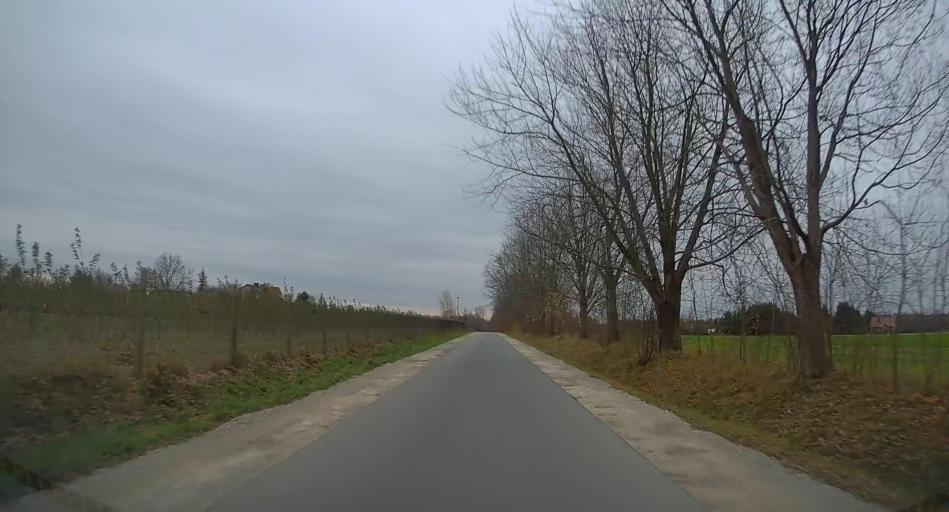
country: PL
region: Lodz Voivodeship
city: Zabia Wola
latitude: 52.0064
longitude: 20.6565
